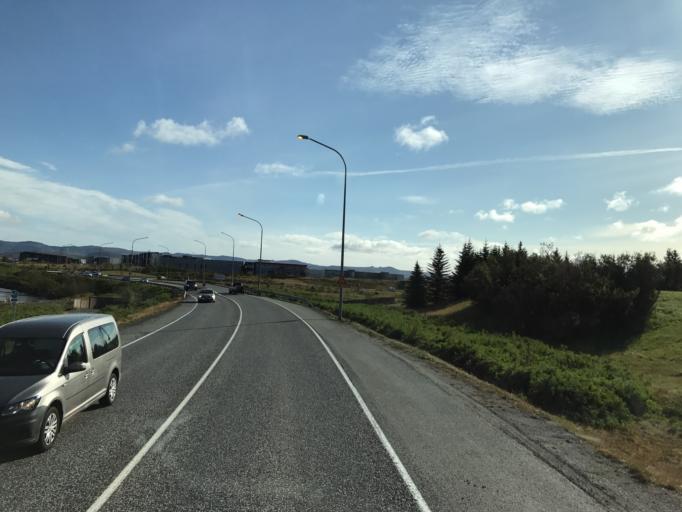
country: IS
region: Capital Region
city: Mosfellsbaer
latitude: 64.1068
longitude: -21.7782
